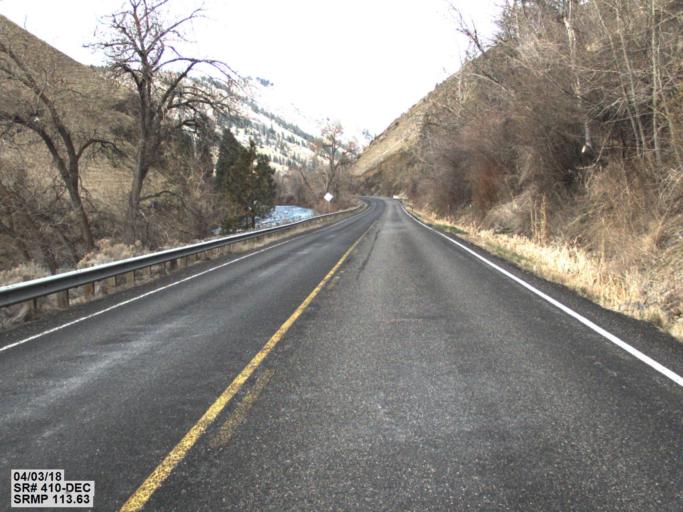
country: US
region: Washington
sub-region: Yakima County
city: Tieton
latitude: 46.7659
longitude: -120.8309
